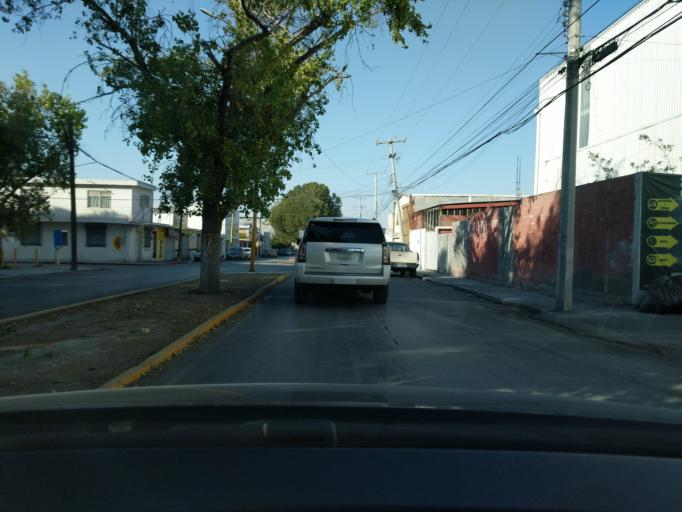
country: MX
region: Coahuila
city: Saltillo
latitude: 25.4697
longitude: -100.9840
